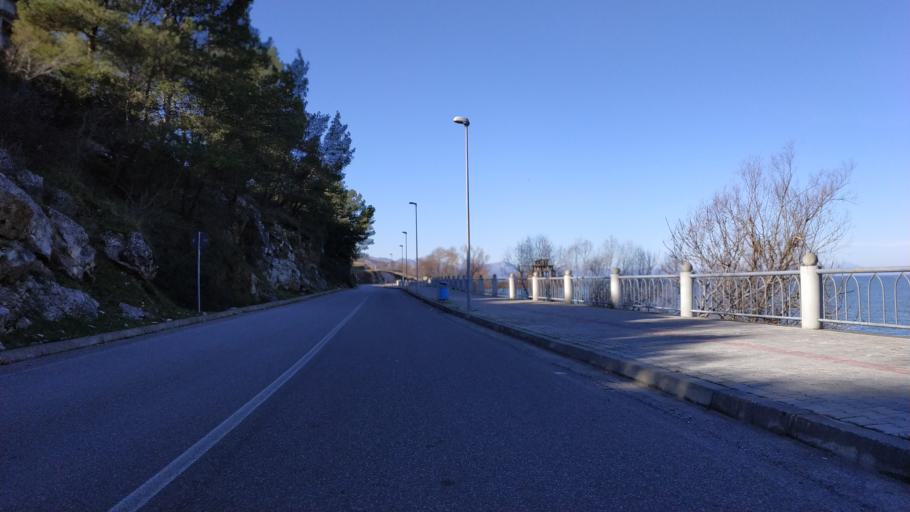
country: AL
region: Shkoder
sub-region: Rrethi i Shkodres
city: Berdica e Madhe
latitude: 42.0574
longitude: 19.4659
